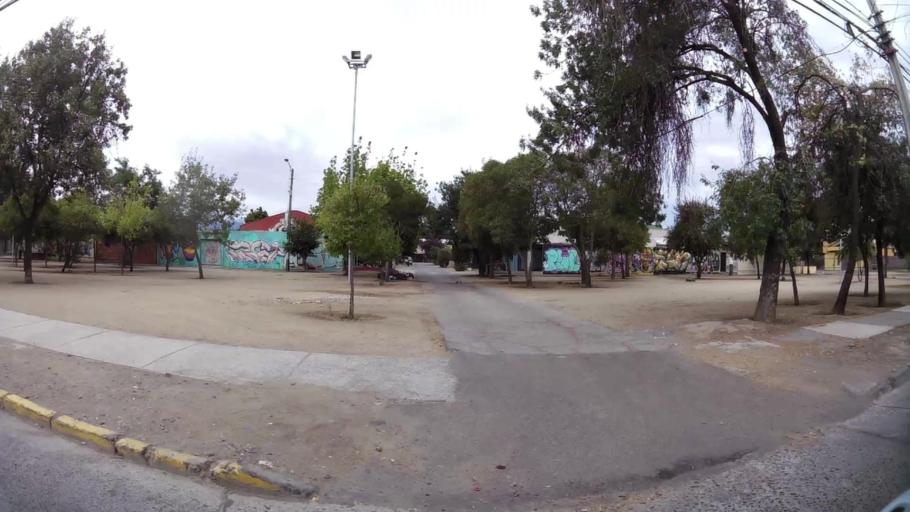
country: CL
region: O'Higgins
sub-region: Provincia de Cachapoal
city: Rancagua
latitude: -34.1575
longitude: -70.7412
